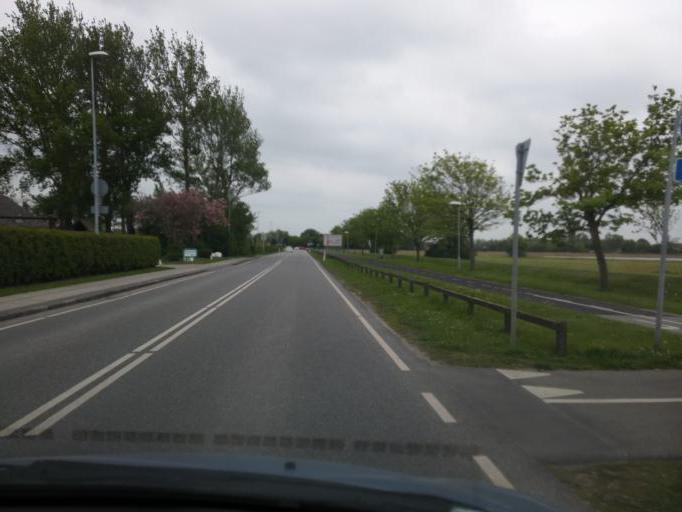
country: DK
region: South Denmark
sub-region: Kerteminde Kommune
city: Kerteminde
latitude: 55.4448
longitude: 10.6579
